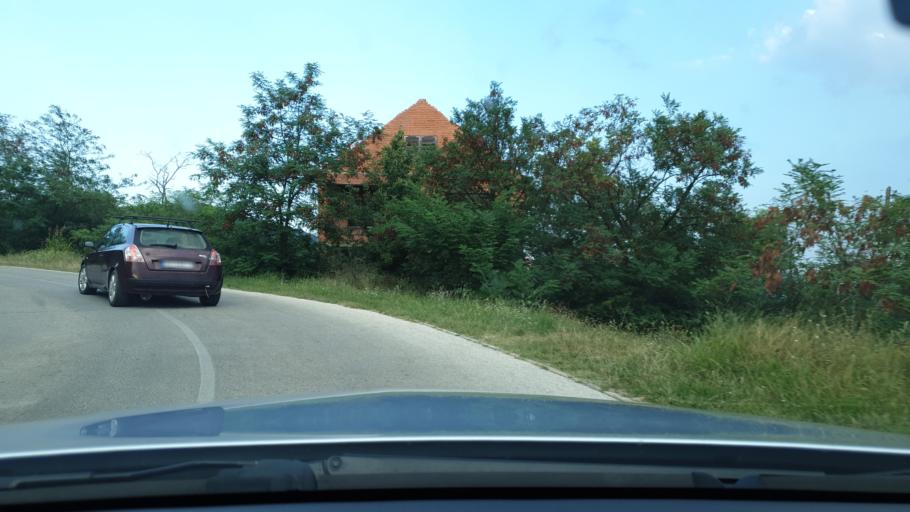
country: RS
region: Autonomna Pokrajina Vojvodina
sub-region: Juznobanatski Okrug
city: Vrsac
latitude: 45.1185
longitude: 21.3248
